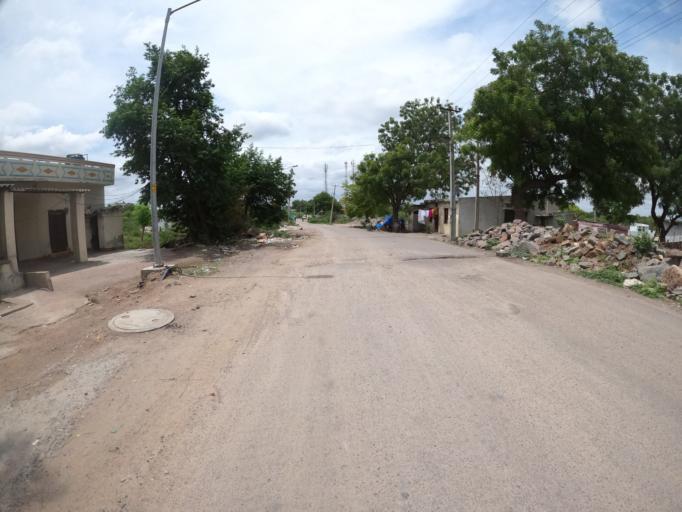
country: IN
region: Telangana
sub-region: Hyderabad
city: Hyderabad
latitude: 17.2984
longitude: 78.3784
